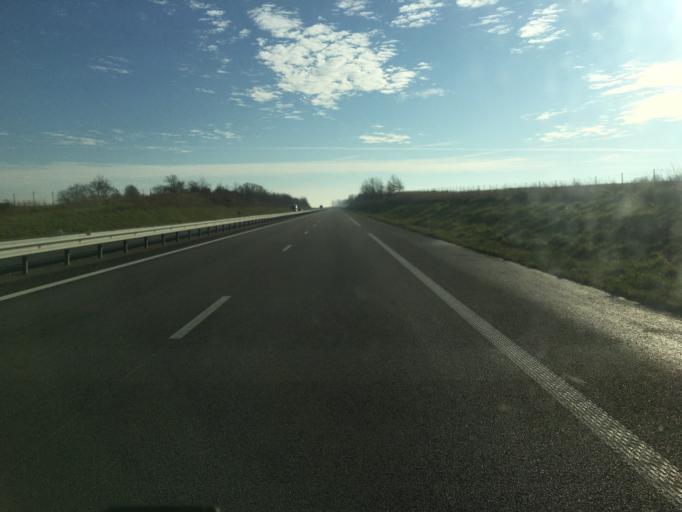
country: FR
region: Haute-Normandie
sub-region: Departement de la Seine-Maritime
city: Limesy
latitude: 49.6556
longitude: 0.9490
